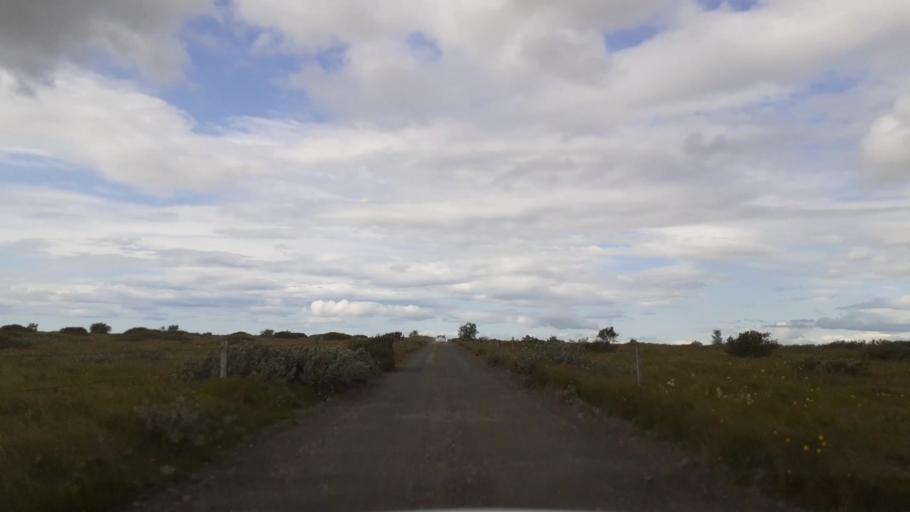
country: IS
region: South
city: Vestmannaeyjar
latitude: 63.8189
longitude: -20.4218
